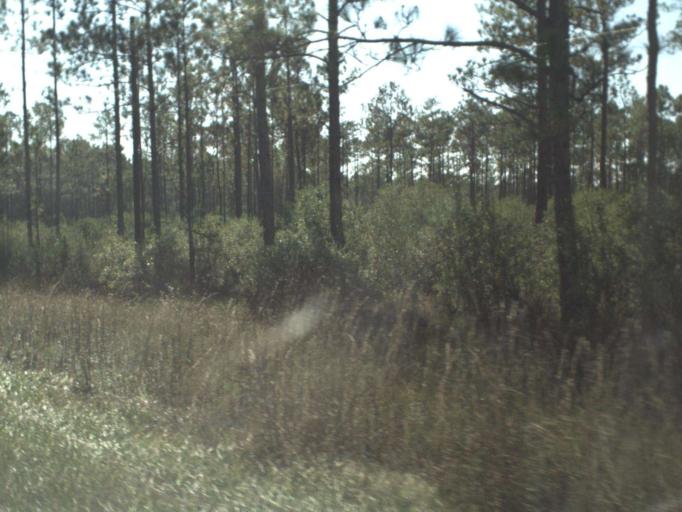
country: US
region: Florida
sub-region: Gulf County
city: Wewahitchka
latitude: 30.0800
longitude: -84.9833
